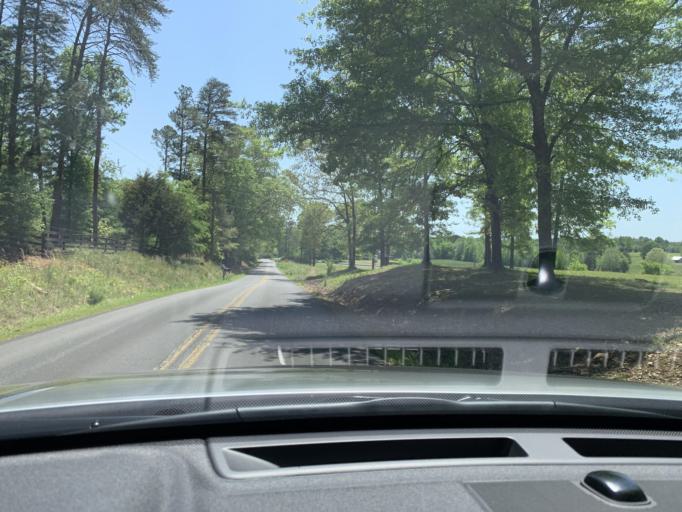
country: US
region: Georgia
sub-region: Polk County
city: Aragon
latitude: 34.0887
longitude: -85.1260
